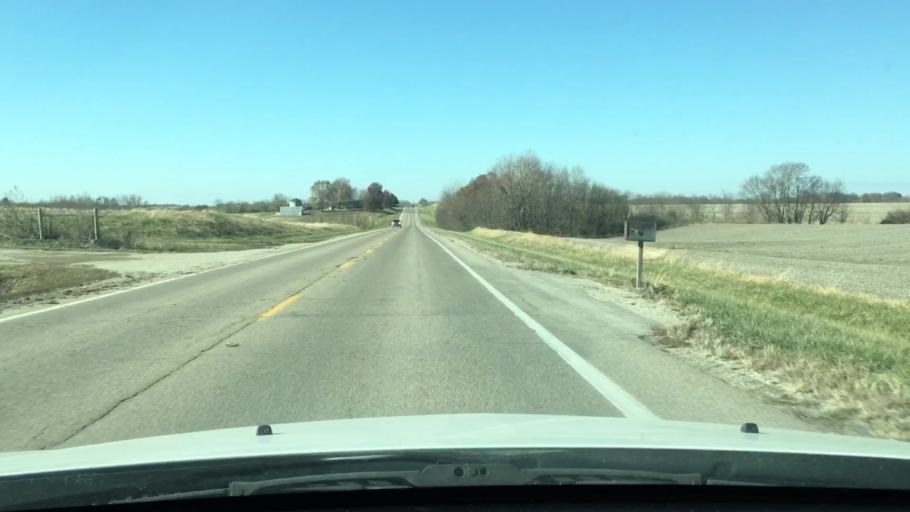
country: US
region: Illinois
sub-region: Pike County
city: Pittsfield
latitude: 39.6050
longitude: -90.8636
